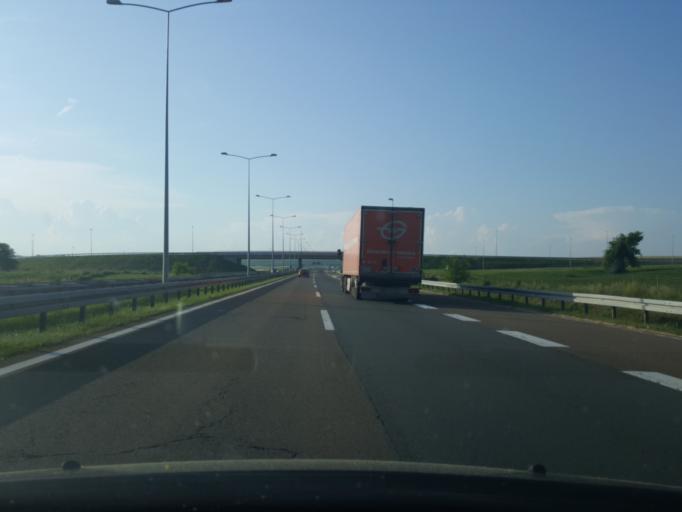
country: RS
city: Beska
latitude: 45.1341
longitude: 20.0885
